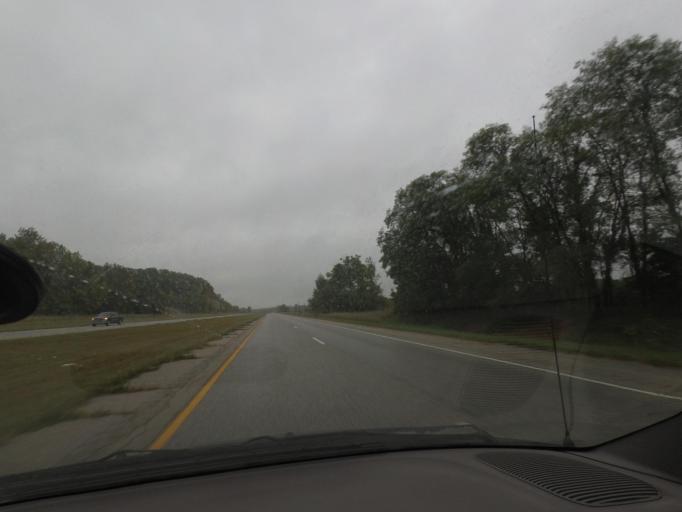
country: US
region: Illinois
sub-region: Pike County
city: Barry
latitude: 39.7133
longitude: -91.0900
